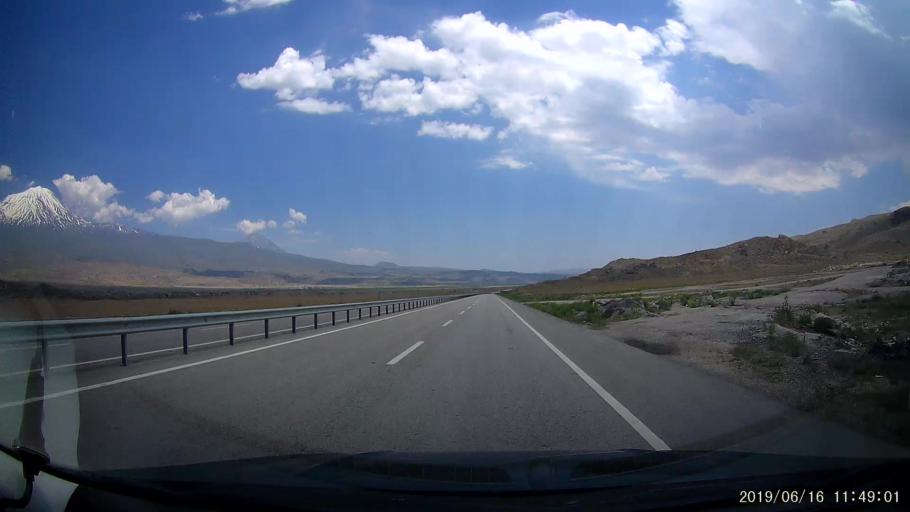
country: TR
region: Agri
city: Dogubayazit
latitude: 39.5577
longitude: 44.1554
